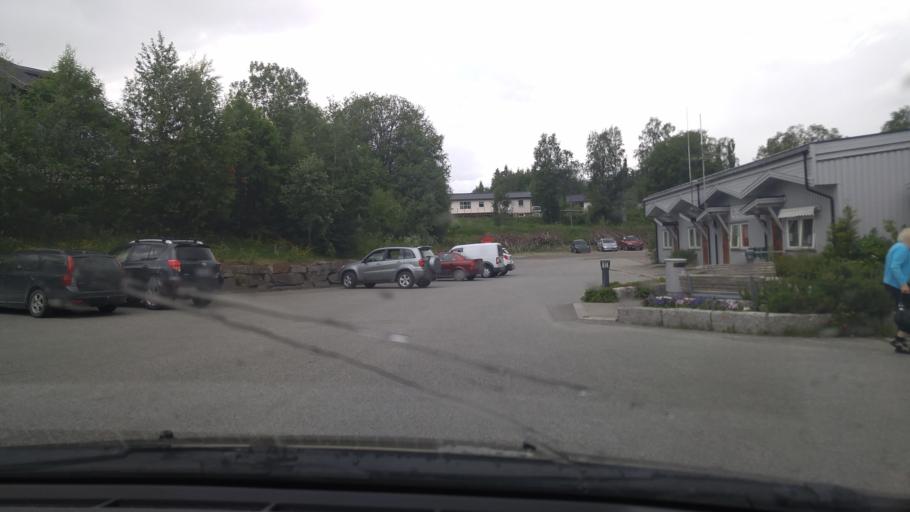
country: NO
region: Nord-Trondelag
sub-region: Namdalseid
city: Namdalseid
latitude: 64.2232
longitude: 11.2230
